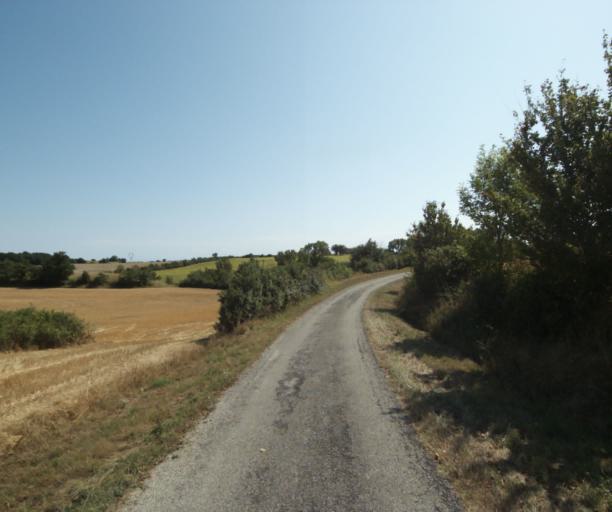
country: FR
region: Midi-Pyrenees
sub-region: Departement de la Haute-Garonne
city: Saint-Felix-Lauragais
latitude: 43.4566
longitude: 1.8467
